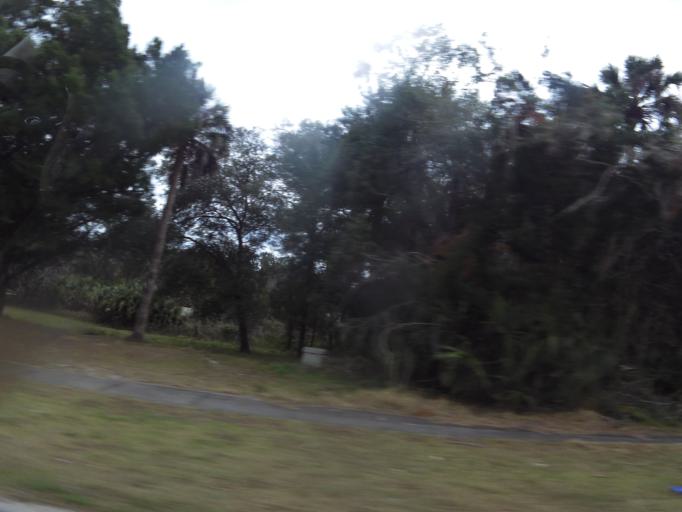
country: US
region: Florida
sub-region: Volusia County
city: Pierson
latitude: 29.3208
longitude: -81.4948
